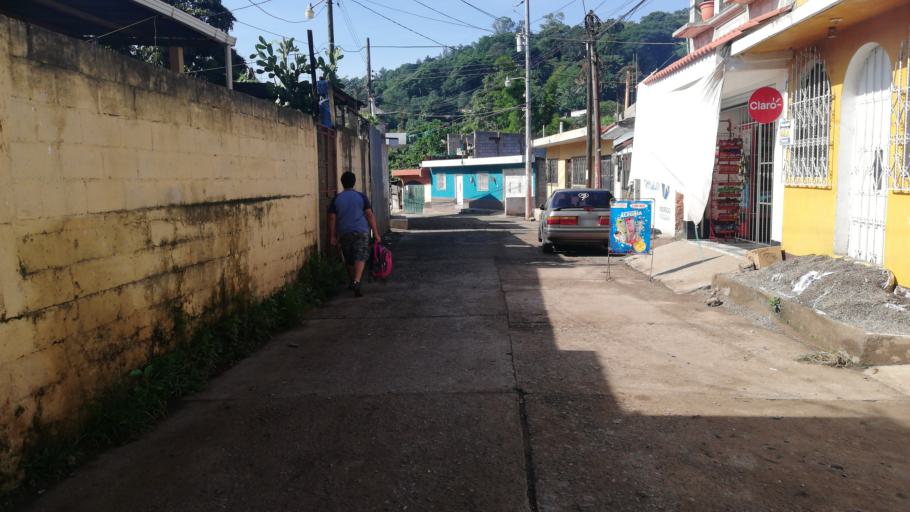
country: GT
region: Santa Rosa
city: Cuilapa
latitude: 14.2803
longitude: -90.3026
